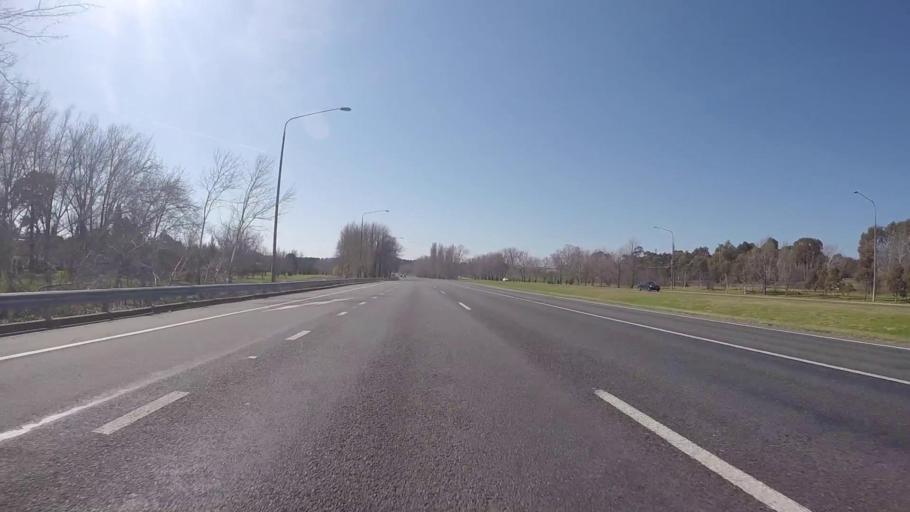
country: AU
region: Australian Capital Territory
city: Forrest
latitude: -35.3241
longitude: 149.0878
